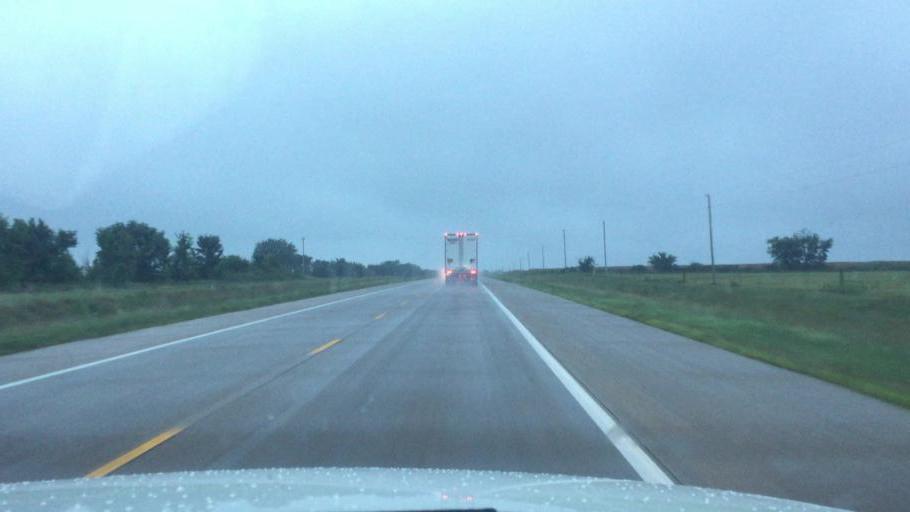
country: US
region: Kansas
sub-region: Neosho County
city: Chanute
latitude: 37.5166
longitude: -95.4710
